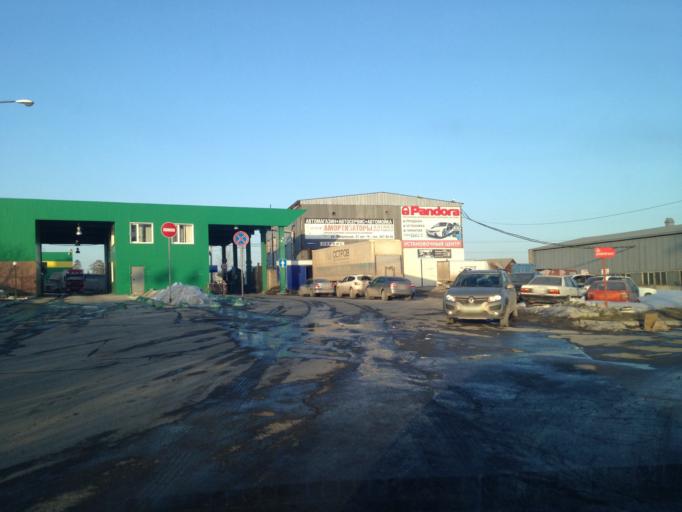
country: RU
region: Sverdlovsk
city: Sovkhoznyy
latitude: 56.7656
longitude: 60.5580
